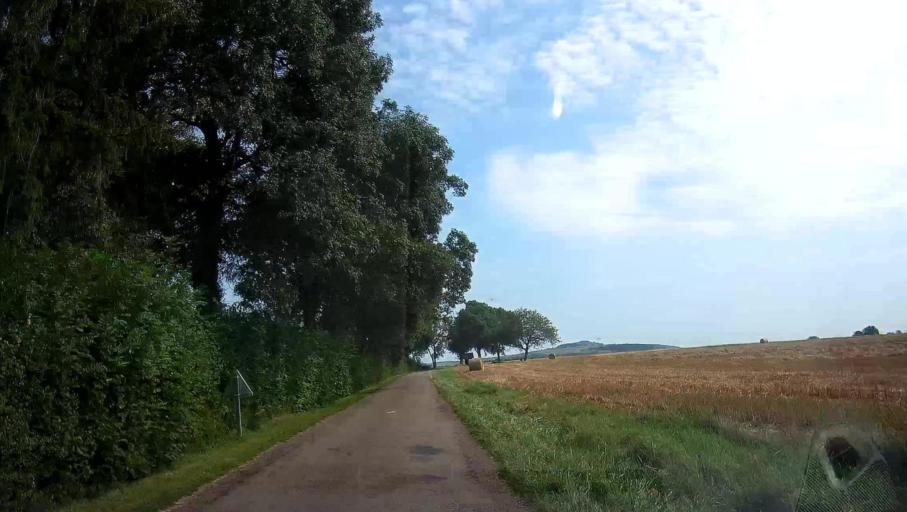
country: FR
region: Bourgogne
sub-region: Departement de Saone-et-Loire
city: Saint-Leger-sur-Dheune
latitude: 46.8981
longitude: 4.6242
